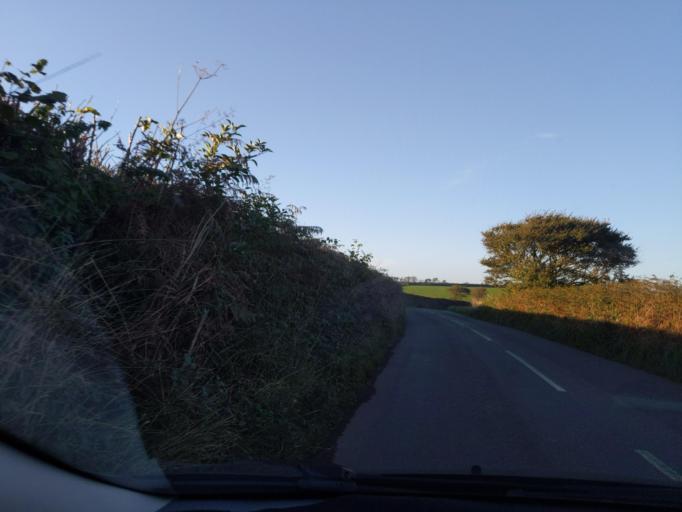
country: GB
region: England
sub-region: Plymouth
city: Plymstock
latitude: 50.3374
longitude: -4.0961
